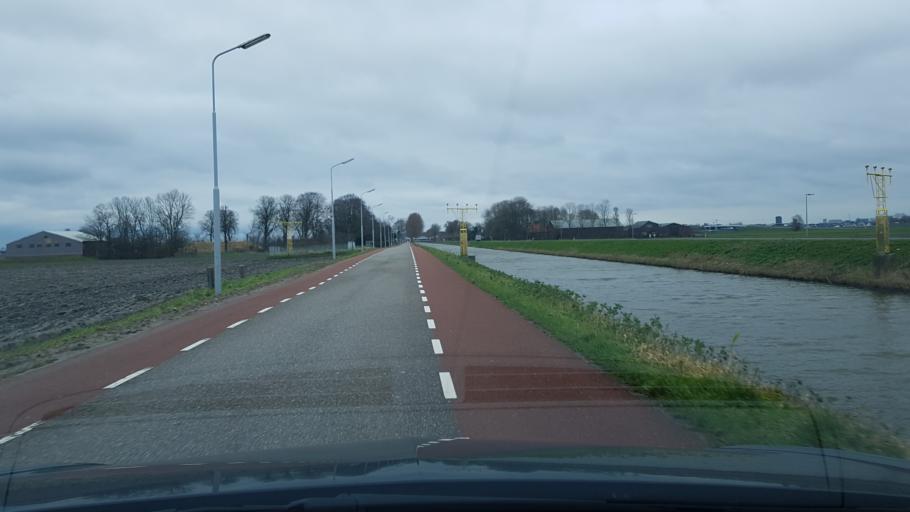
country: NL
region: North Holland
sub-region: Gemeente Haarlemmermeer
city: Hoofddorp
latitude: 52.3386
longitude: 4.7401
